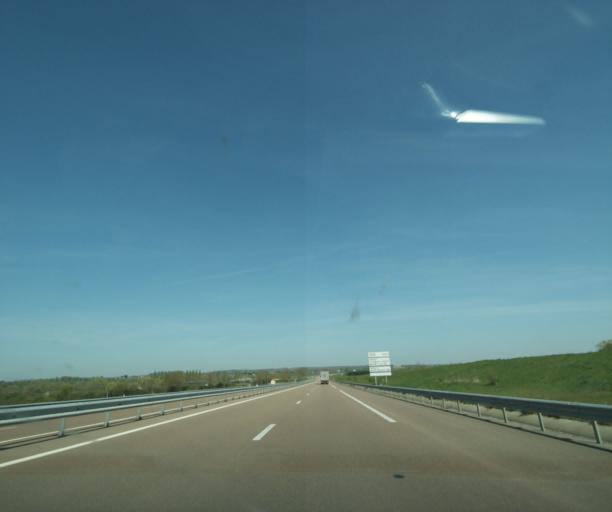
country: FR
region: Bourgogne
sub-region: Departement de la Nievre
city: Magny-Cours
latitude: 46.8615
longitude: 3.1486
